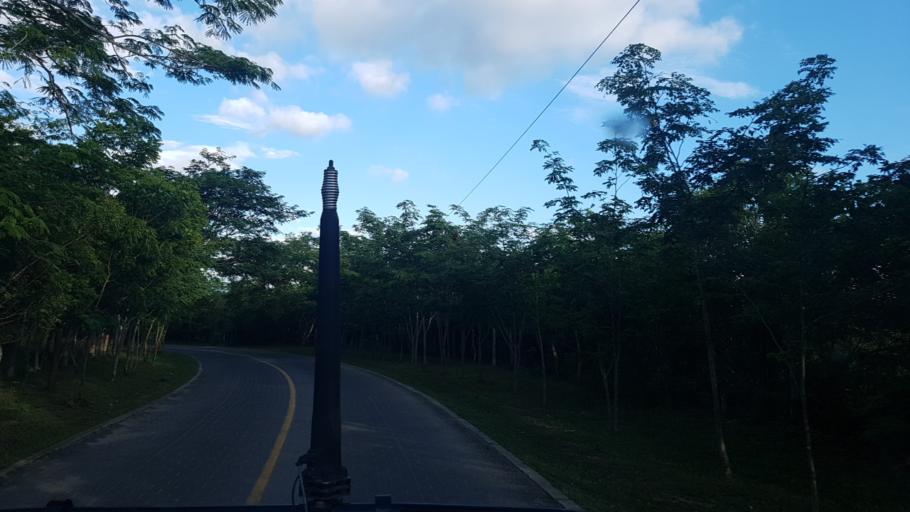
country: NI
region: Nueva Segovia
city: Ocotal
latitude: 13.6433
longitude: -86.6015
